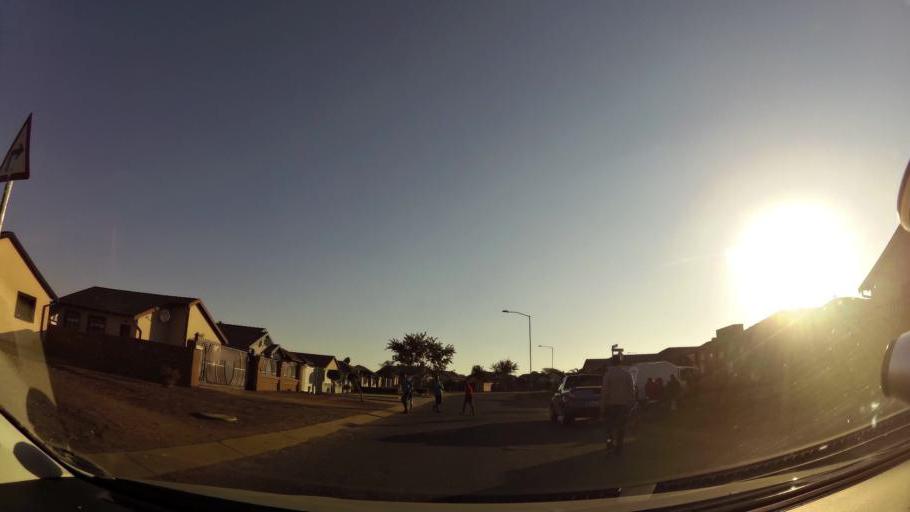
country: ZA
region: Gauteng
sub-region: City of Tshwane Metropolitan Municipality
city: Pretoria
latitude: -25.7429
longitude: 28.1156
